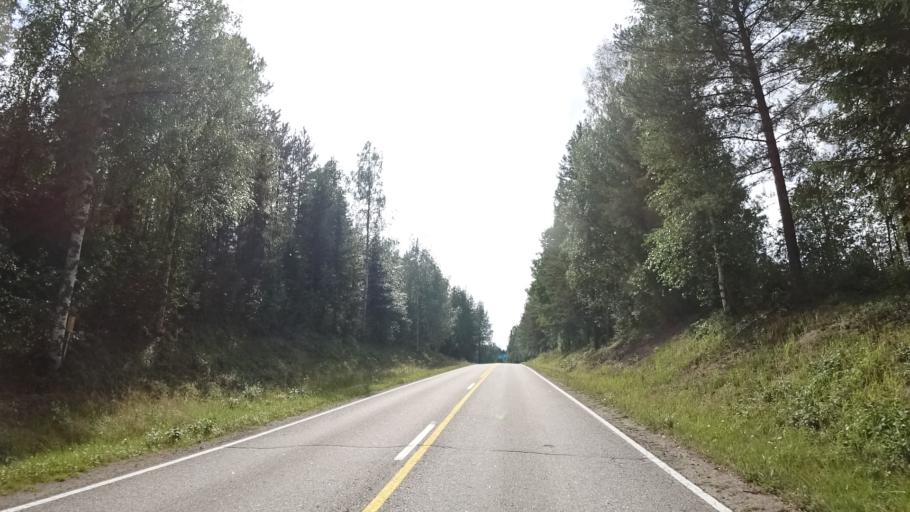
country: FI
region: North Karelia
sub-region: Joensuu
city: Ilomantsi
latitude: 62.7556
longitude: 31.0038
